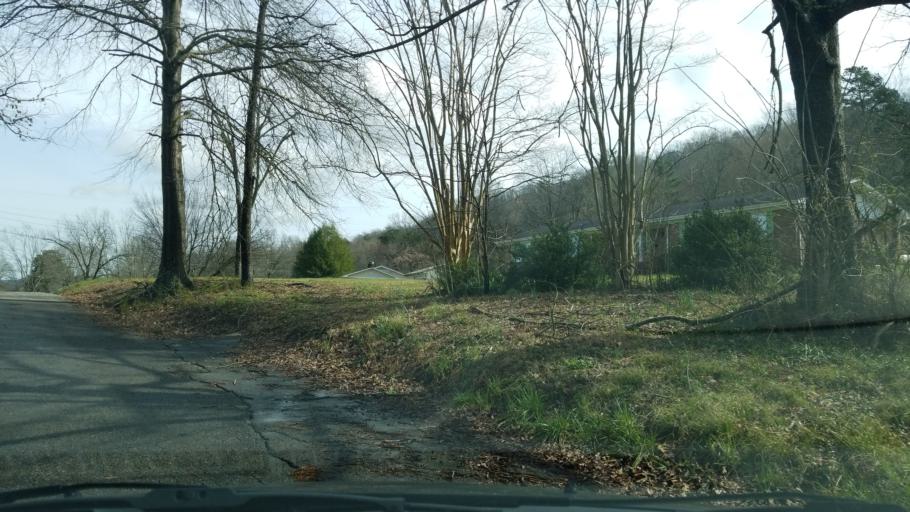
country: US
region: Tennessee
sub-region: Hamilton County
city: Collegedale
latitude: 35.0687
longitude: -85.0586
